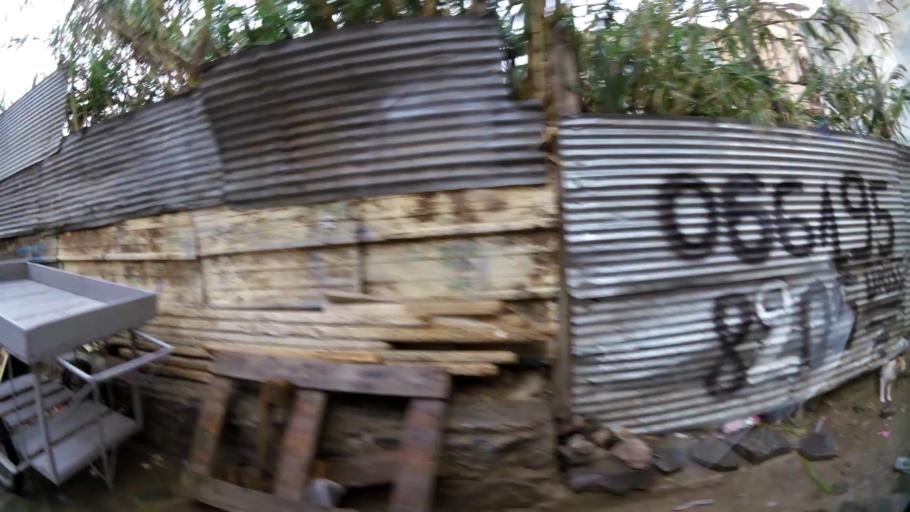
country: MA
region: Oriental
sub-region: Nador
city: Nador
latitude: 35.1755
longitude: -2.9374
